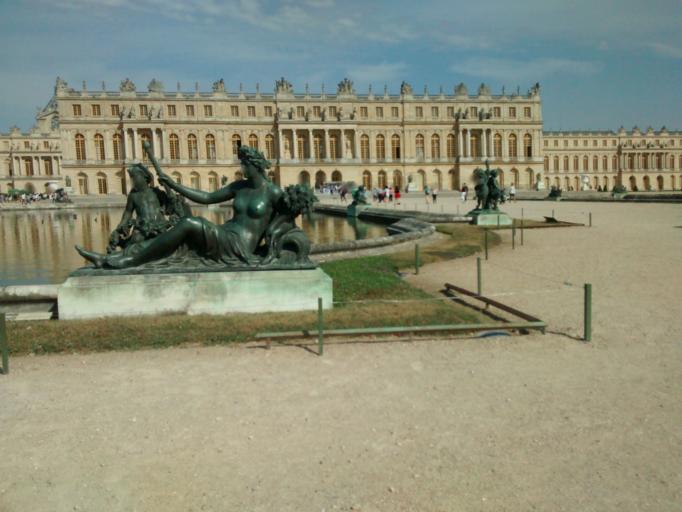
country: FR
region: Ile-de-France
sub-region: Departement des Yvelines
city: Versailles
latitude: 48.8054
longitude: 2.1187
